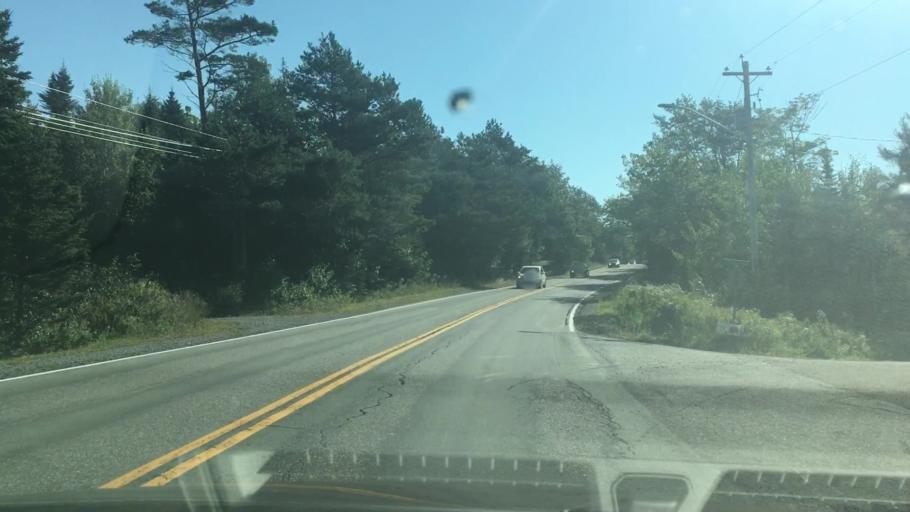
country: CA
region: Nova Scotia
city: Cole Harbour
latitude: 44.7782
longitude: -63.0612
